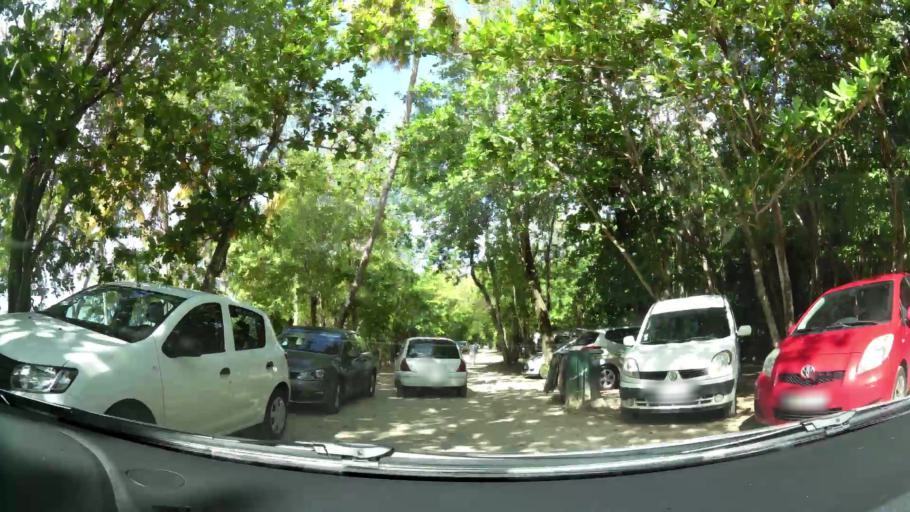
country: MQ
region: Martinique
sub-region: Martinique
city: Le Marin
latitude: 14.4033
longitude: -60.8783
